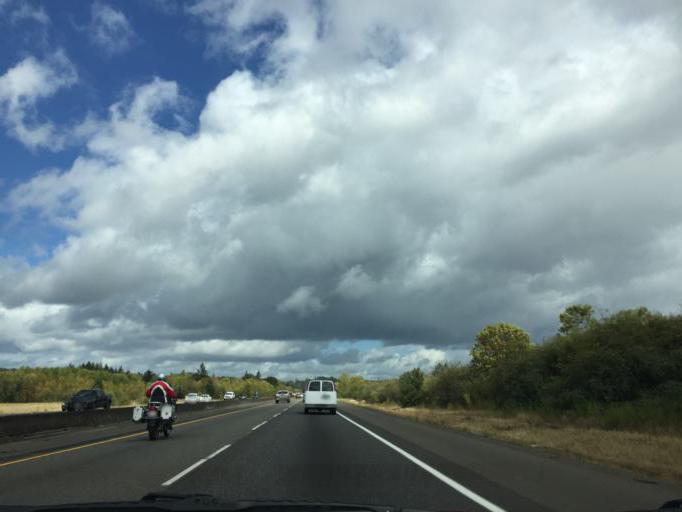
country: US
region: Washington
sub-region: Lewis County
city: Winlock
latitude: 46.4574
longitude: -122.8859
